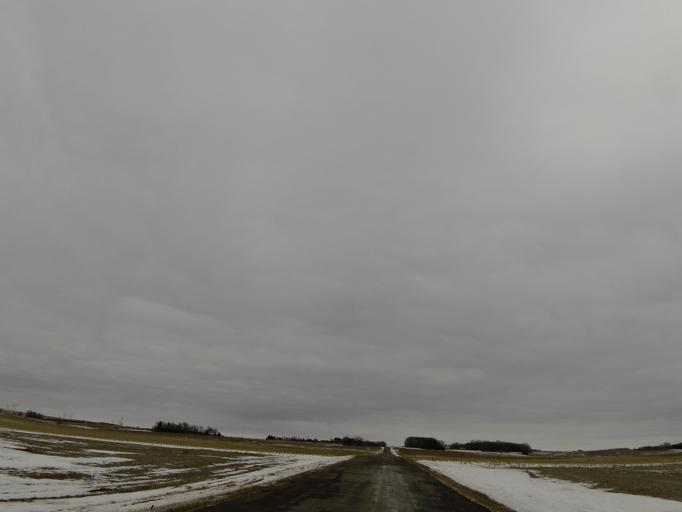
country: US
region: Minnesota
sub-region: Washington County
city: Cottage Grove
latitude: 44.8046
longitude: -92.8891
